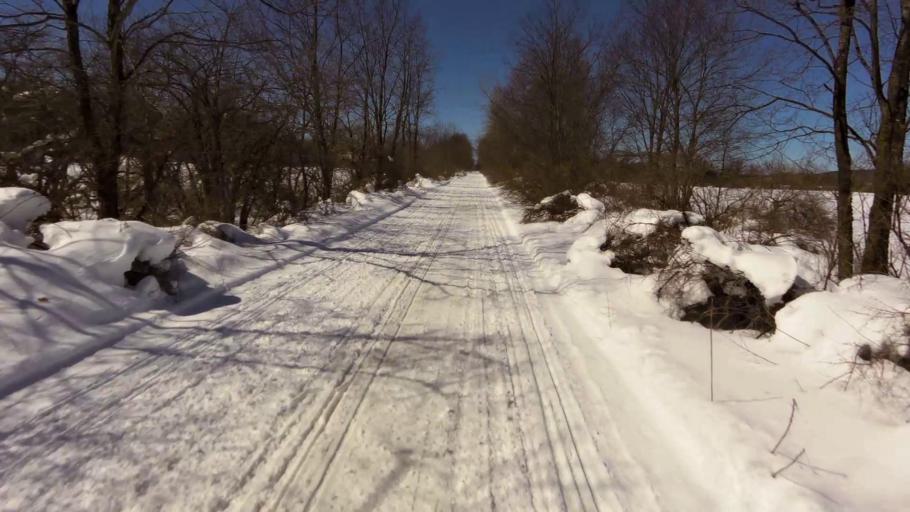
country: US
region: New York
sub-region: Cattaraugus County
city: Delevan
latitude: 42.4365
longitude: -78.4110
